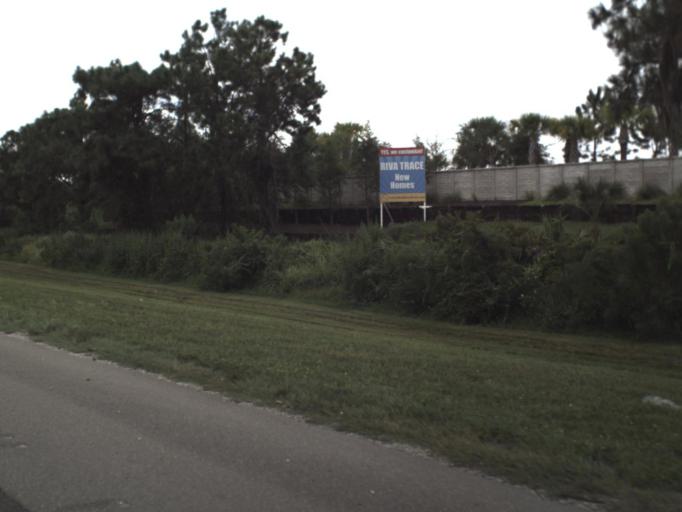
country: US
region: Florida
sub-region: Sarasota County
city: The Meadows
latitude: 27.4113
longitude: -82.4553
